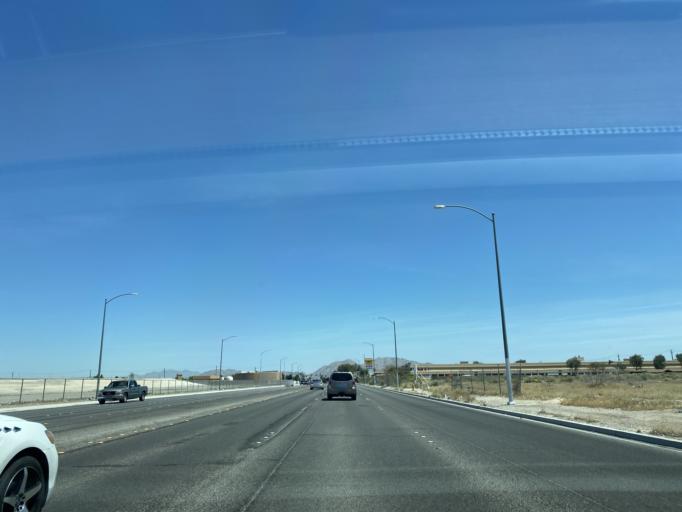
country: US
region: Nevada
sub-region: Clark County
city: Las Vegas
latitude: 36.1975
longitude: -115.1838
